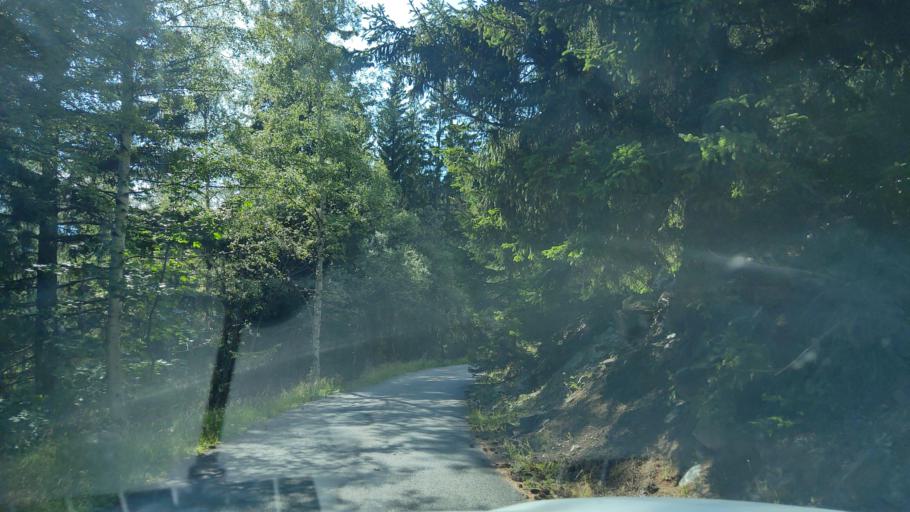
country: FR
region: Rhone-Alpes
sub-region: Departement de la Savoie
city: Val Thorens
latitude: 45.2209
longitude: 6.5592
